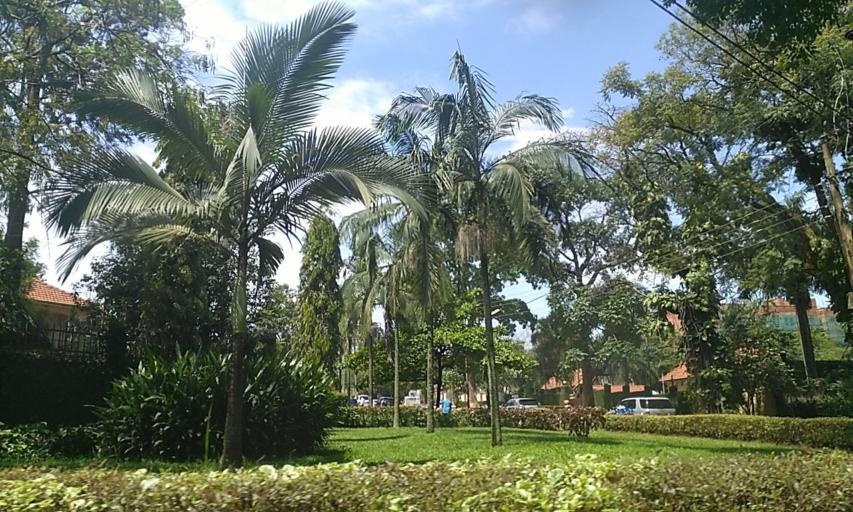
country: UG
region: Central Region
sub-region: Kampala District
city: Kampala
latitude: 0.3274
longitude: 32.6026
